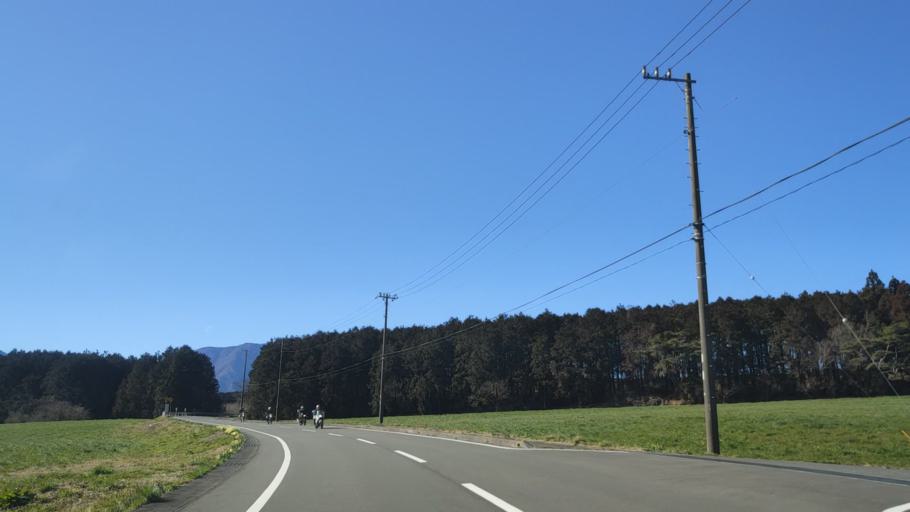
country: JP
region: Yamanashi
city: Fujikawaguchiko
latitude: 35.3676
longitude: 138.6037
